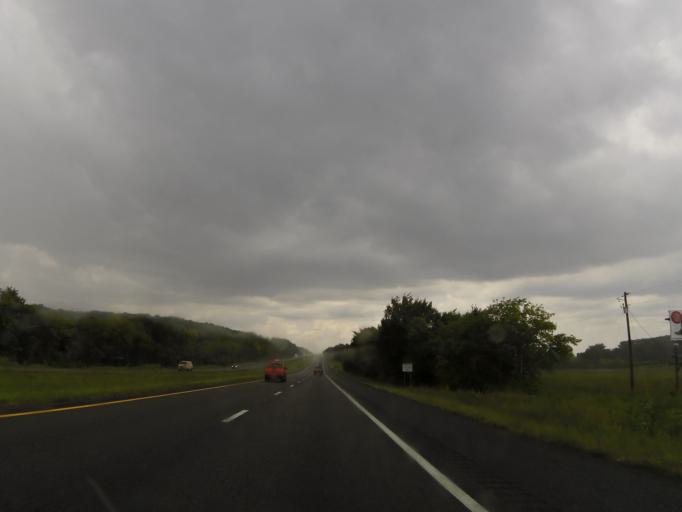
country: US
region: Tennessee
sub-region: Wilson County
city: Lebanon
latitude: 36.1944
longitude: -86.2053
